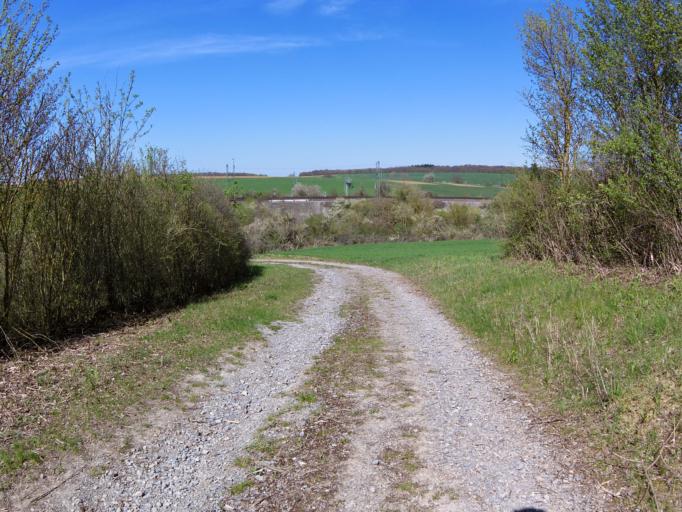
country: DE
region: Bavaria
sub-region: Regierungsbezirk Unterfranken
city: Rottendorf
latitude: 49.7987
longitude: 10.0359
